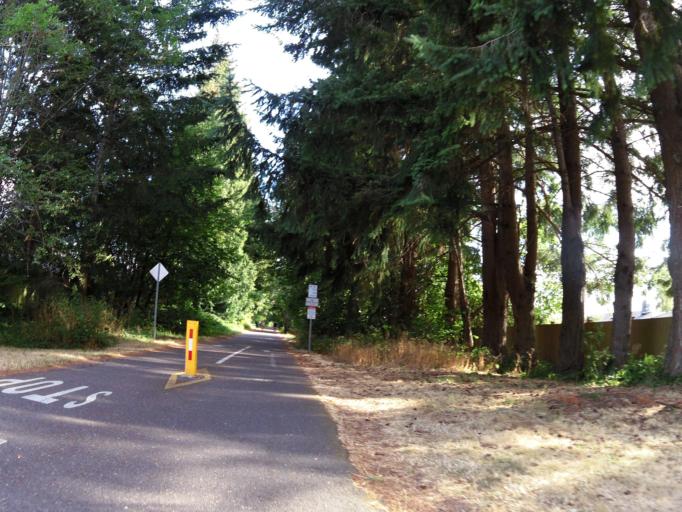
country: US
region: Washington
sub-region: Thurston County
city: Lacey
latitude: 47.0278
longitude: -122.8366
